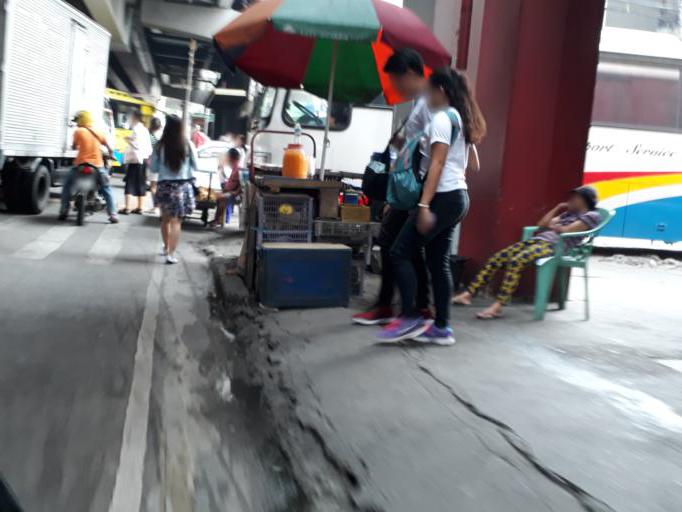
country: PH
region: Metro Manila
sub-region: City of Manila
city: Manila
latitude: 14.6049
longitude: 120.9822
